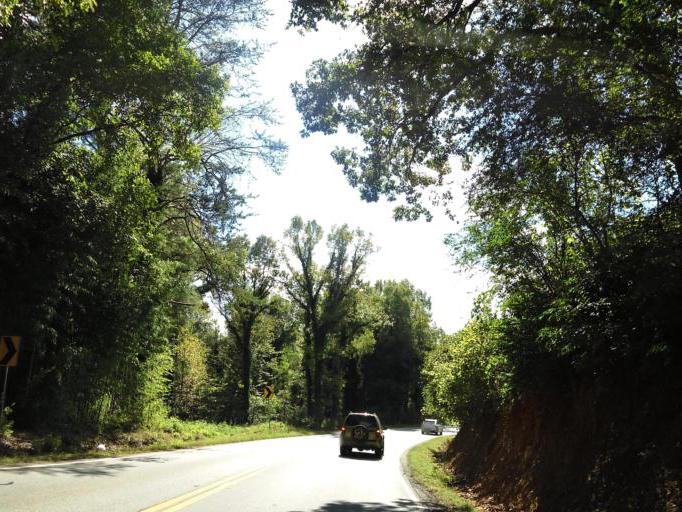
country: US
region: Georgia
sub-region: Pickens County
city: Nelson
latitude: 34.4156
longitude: -84.3642
